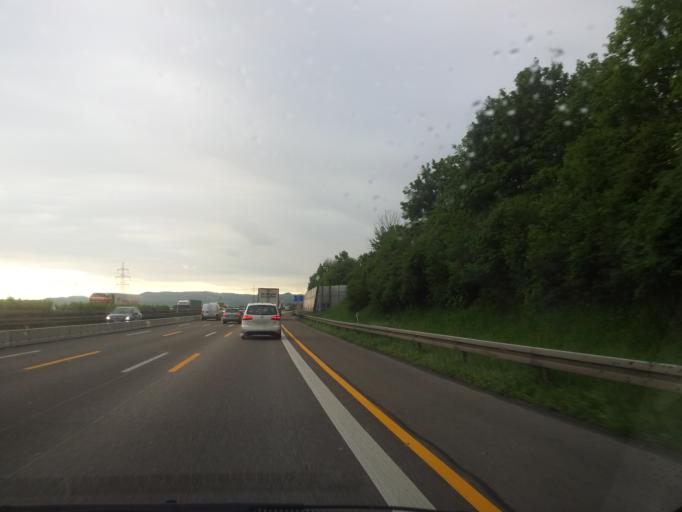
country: DE
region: Baden-Wuerttemberg
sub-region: Regierungsbezirk Stuttgart
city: Kirchheim unter Teck
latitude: 48.6492
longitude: 9.4143
